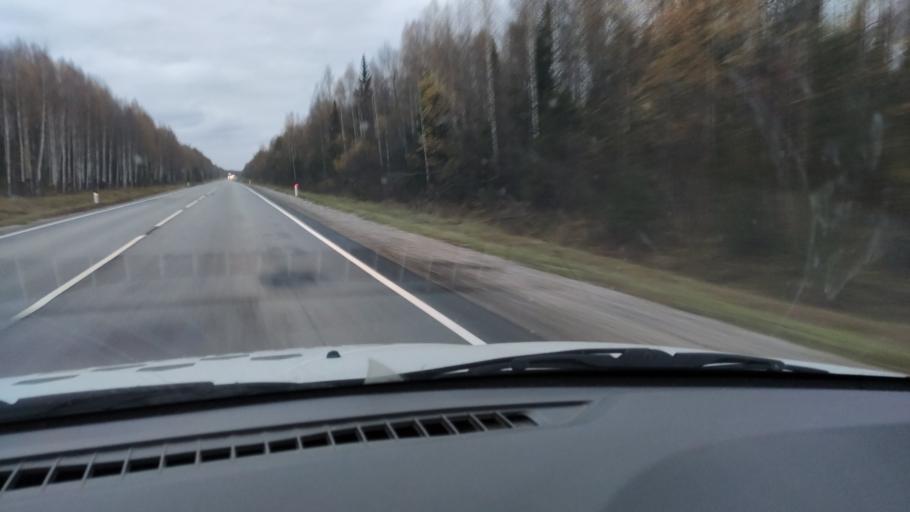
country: RU
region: Kirov
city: Kostino
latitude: 58.8102
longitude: 52.9295
